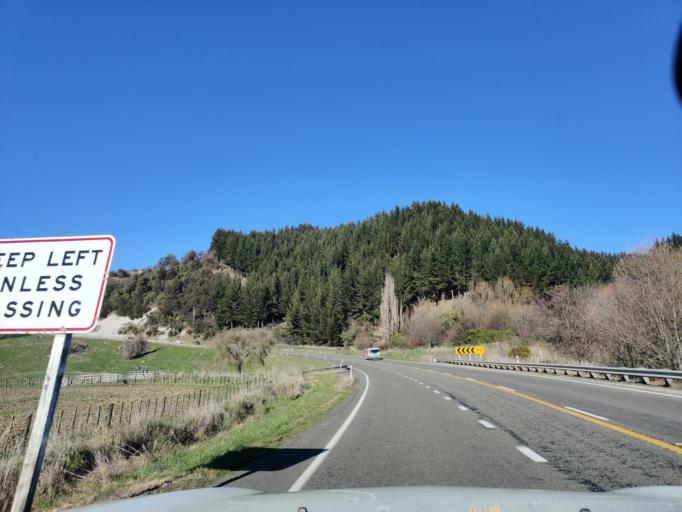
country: NZ
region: Manawatu-Wanganui
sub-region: Ruapehu District
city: Waiouru
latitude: -39.8217
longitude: 175.7768
